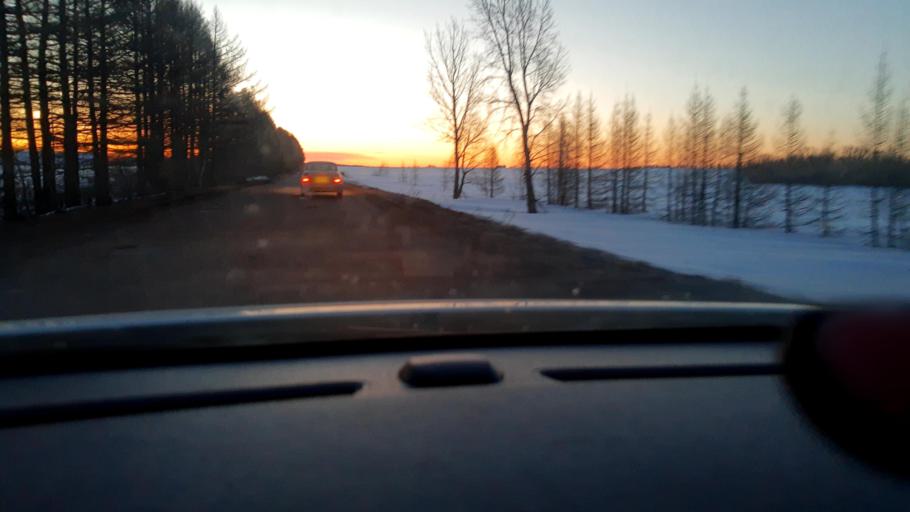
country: RU
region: Bashkortostan
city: Avdon
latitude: 54.3877
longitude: 55.7244
